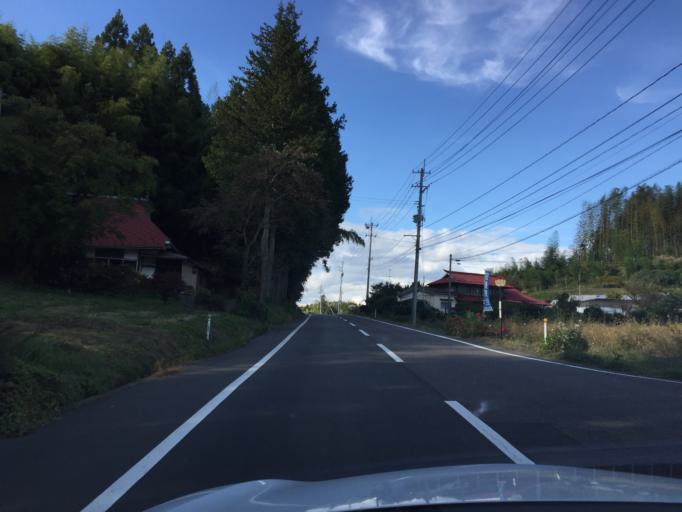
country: JP
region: Fukushima
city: Ishikawa
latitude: 37.1982
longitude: 140.4591
